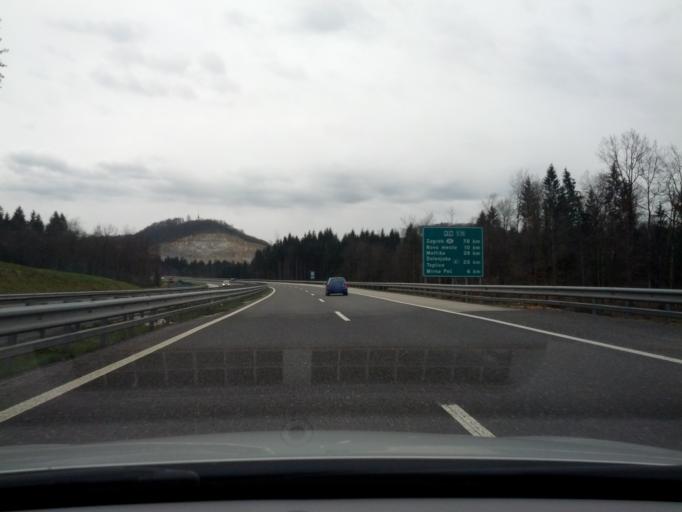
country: SI
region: Trebnje
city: Trebnje
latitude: 45.8945
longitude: 15.0580
